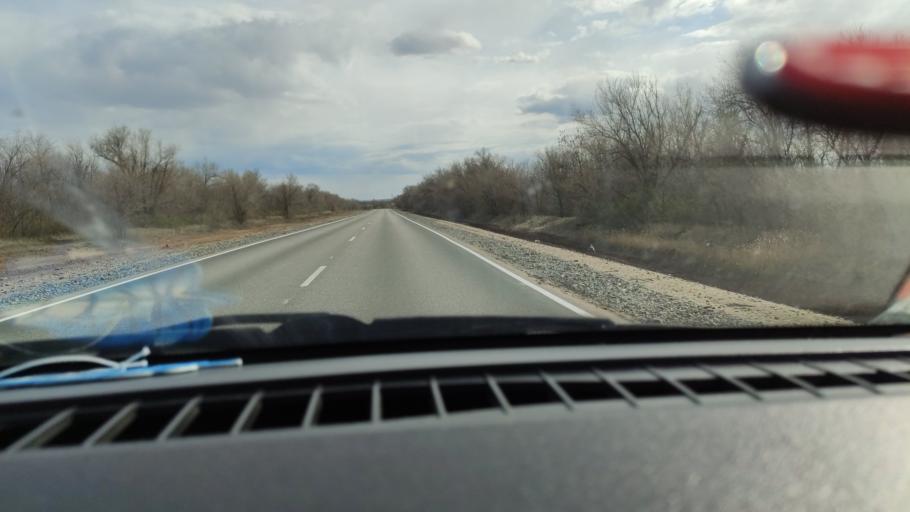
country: RU
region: Saratov
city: Krasnoarmeysk
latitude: 51.1220
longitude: 45.9572
